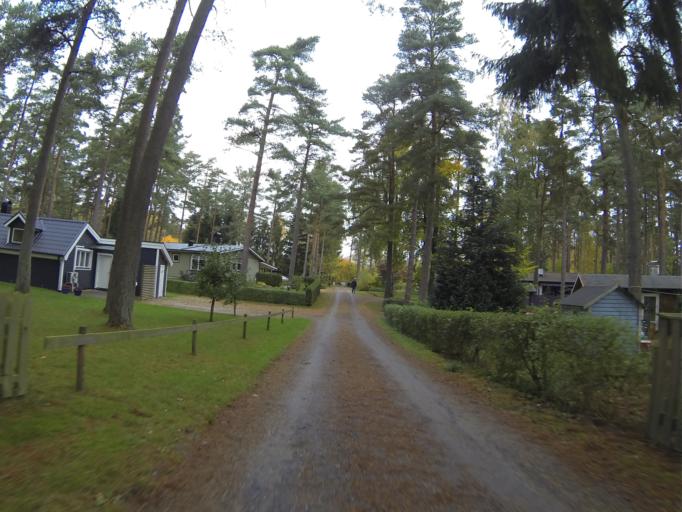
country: SE
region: Skane
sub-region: Sjobo Kommun
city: Sjoebo
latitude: 55.6327
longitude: 13.6650
